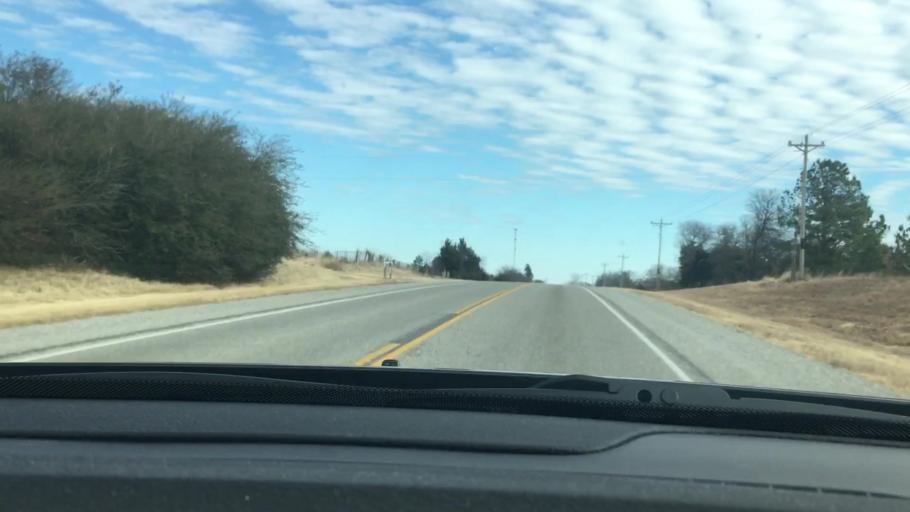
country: US
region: Oklahoma
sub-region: Garvin County
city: Stratford
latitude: 34.7965
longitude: -97.0611
